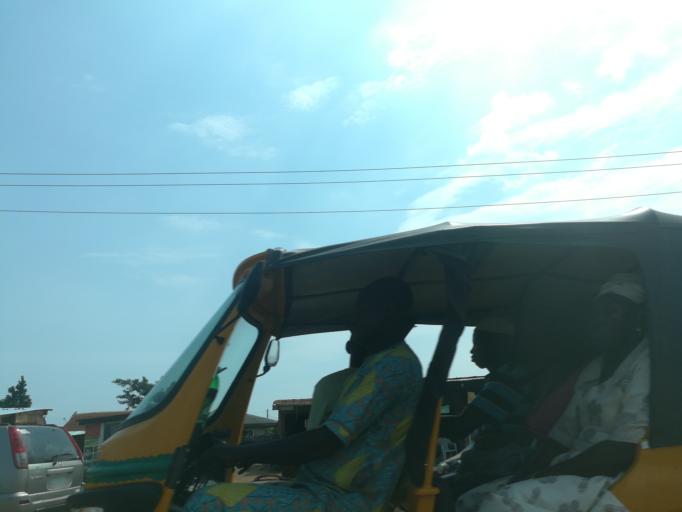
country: NG
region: Lagos
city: Ikorodu
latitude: 6.6013
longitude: 3.6231
